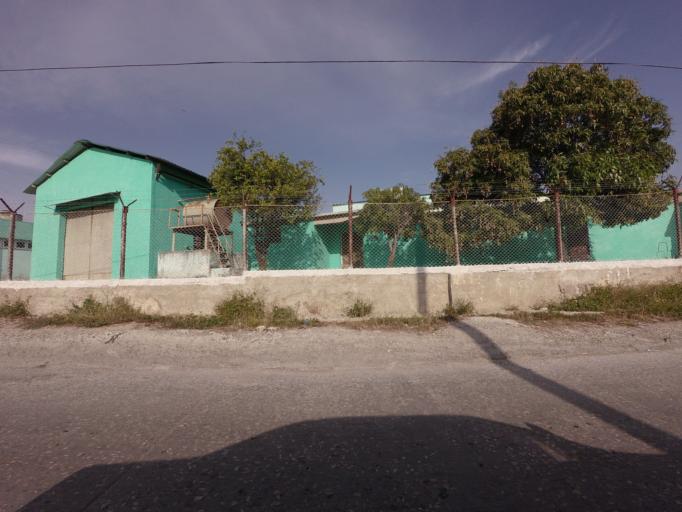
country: CU
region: La Habana
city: Regla
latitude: 23.1083
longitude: -82.3406
